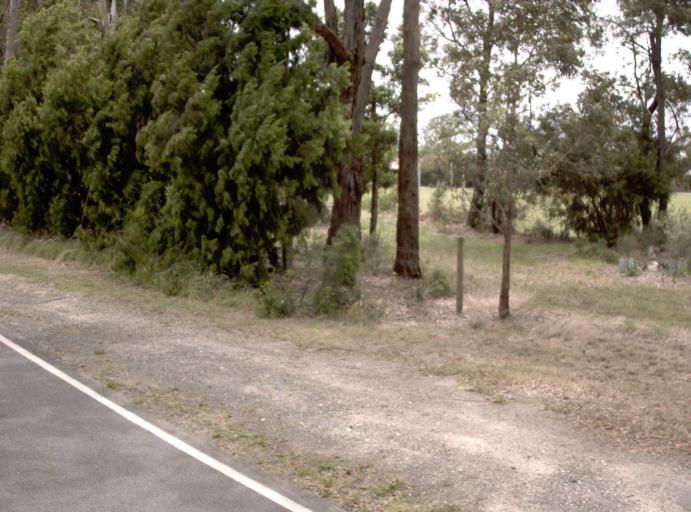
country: AU
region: Victoria
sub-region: Latrobe
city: Moe
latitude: -38.0712
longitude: 146.1753
